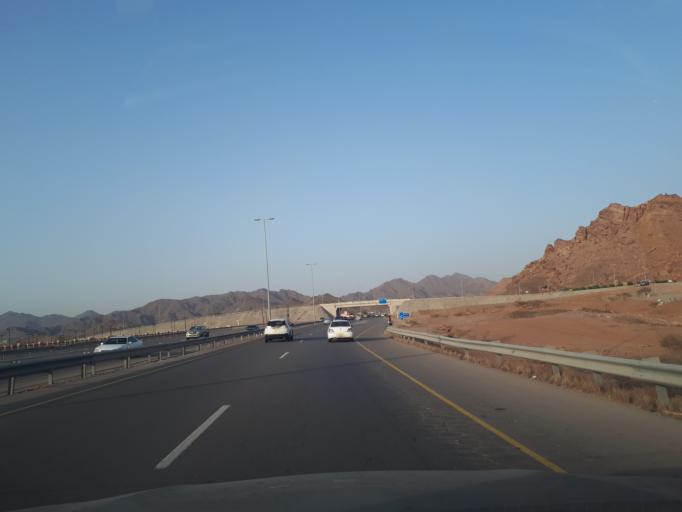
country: OM
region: Muhafazat ad Dakhiliyah
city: Bidbid
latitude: 23.4645
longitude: 58.1241
